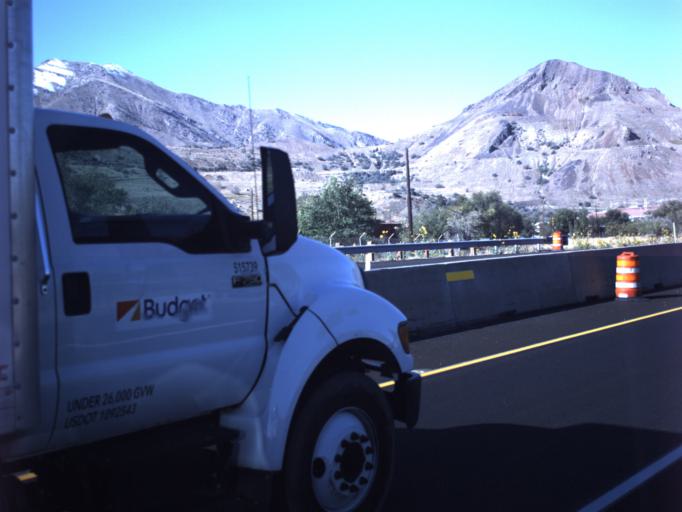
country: US
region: Utah
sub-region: Salt Lake County
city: Magna
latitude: 40.7217
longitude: -112.1558
